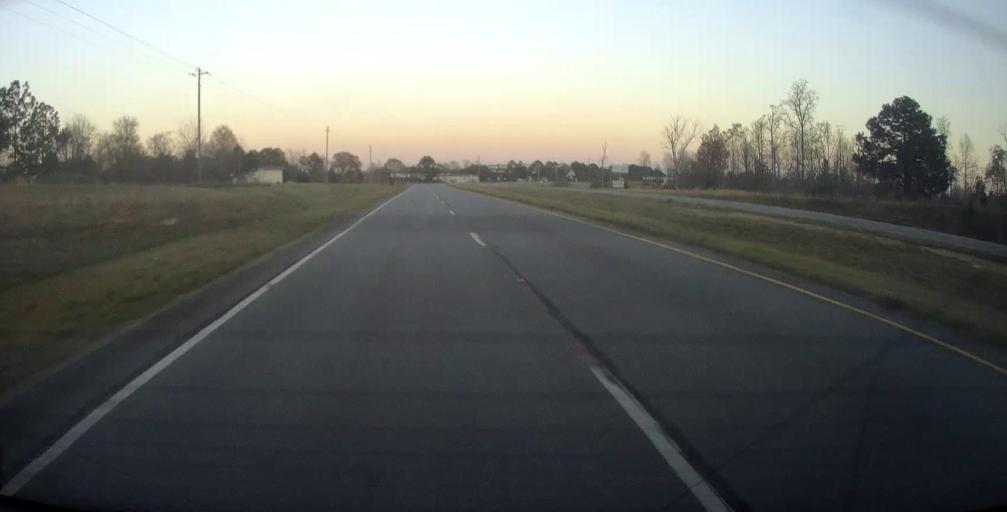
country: US
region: Georgia
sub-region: Dodge County
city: Eastman
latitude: 32.1753
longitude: -83.1653
